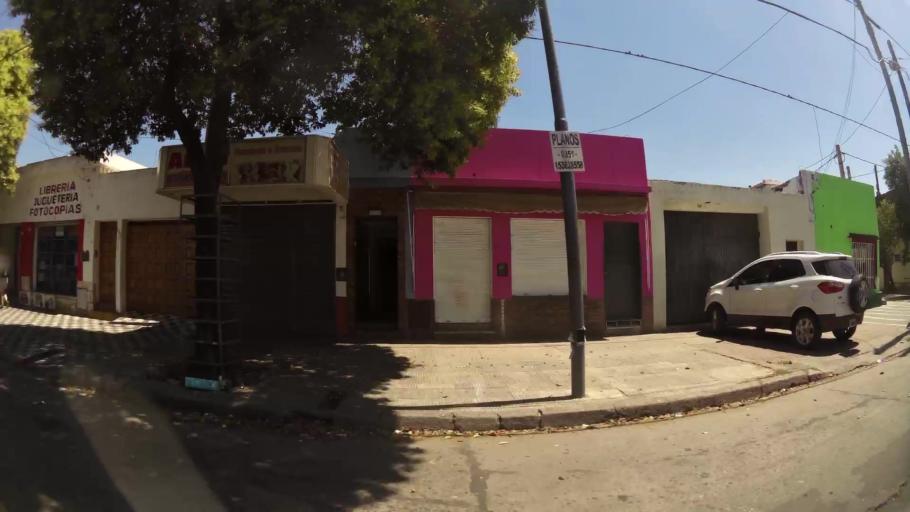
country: AR
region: Cordoba
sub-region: Departamento de Capital
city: Cordoba
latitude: -31.3816
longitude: -64.2003
